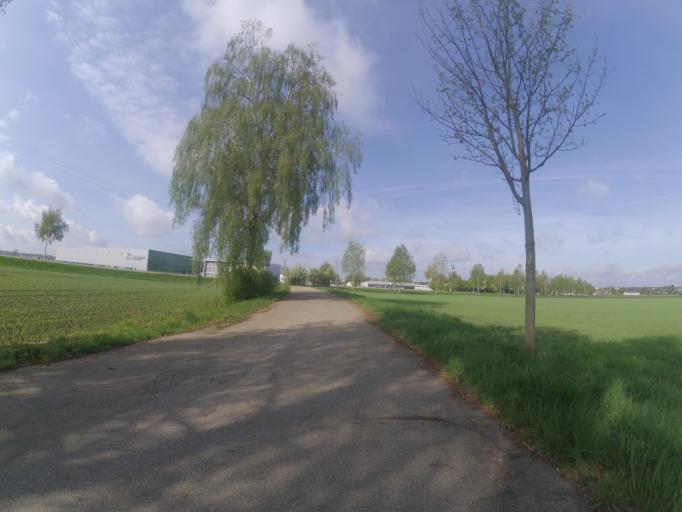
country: DE
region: Baden-Wuerttemberg
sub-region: Tuebingen Region
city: Laupheim
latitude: 48.2295
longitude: 9.8391
